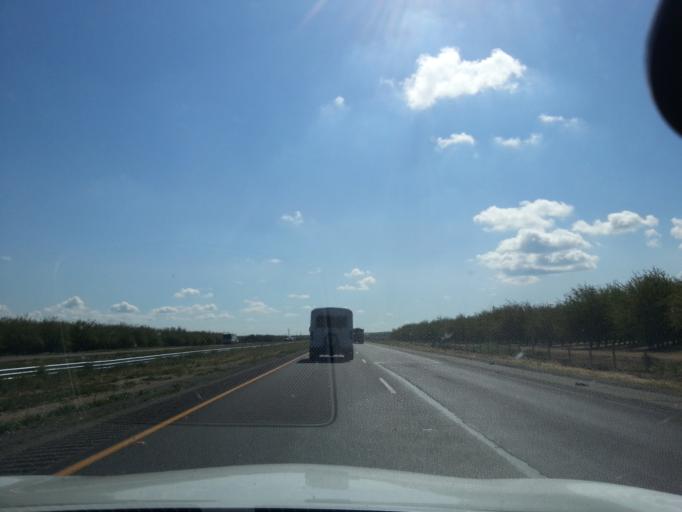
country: US
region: California
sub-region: Fresno County
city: Coalinga
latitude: 36.3974
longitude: -120.3601
